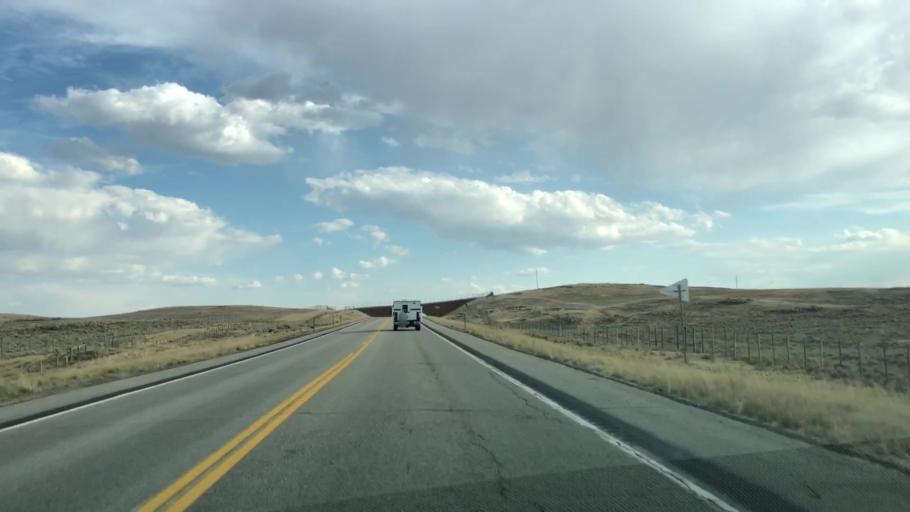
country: US
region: Wyoming
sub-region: Sublette County
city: Pinedale
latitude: 42.9173
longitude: -110.0795
